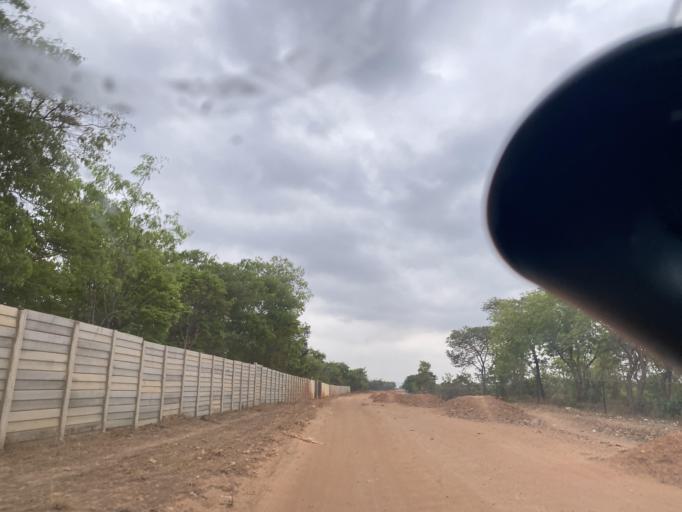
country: ZM
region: Lusaka
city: Chongwe
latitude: -15.2788
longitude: 28.7301
